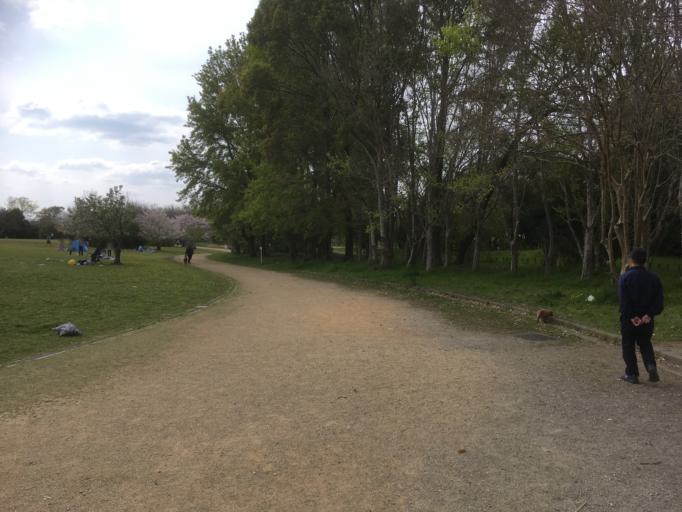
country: JP
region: Nara
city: Tawaramoto
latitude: 34.5978
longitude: 135.7825
